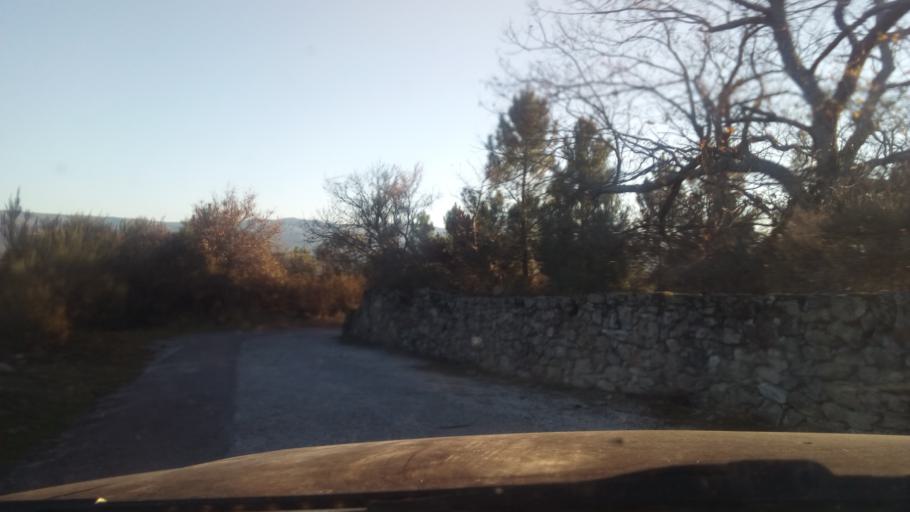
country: PT
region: Guarda
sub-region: Fornos de Algodres
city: Fornos de Algodres
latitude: 40.6070
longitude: -7.5034
